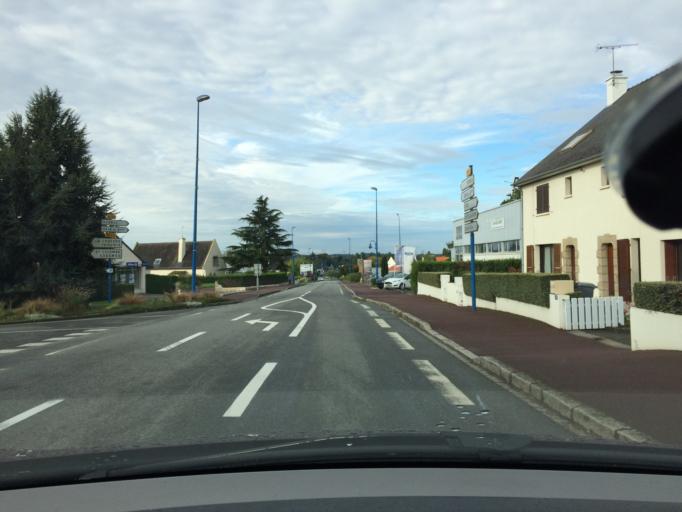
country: FR
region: Brittany
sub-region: Departement d'Ille-et-Vilaine
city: Janze
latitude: 47.9565
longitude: -1.5003
